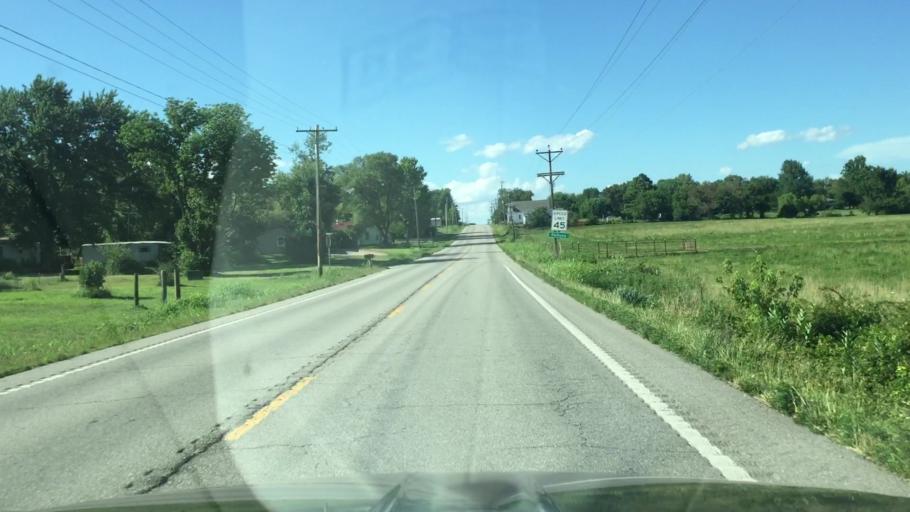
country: US
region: Missouri
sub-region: Moniteau County
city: Tipton
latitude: 38.5633
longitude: -92.7972
